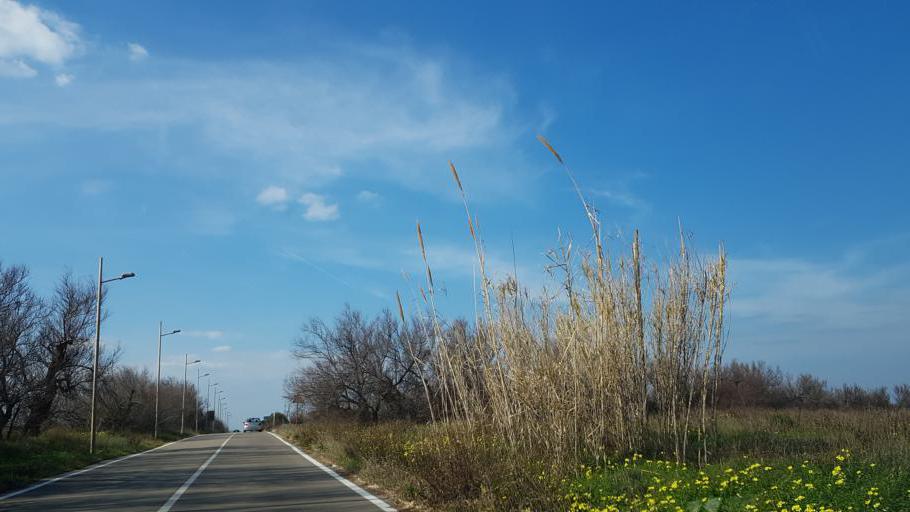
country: IT
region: Apulia
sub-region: Provincia di Brindisi
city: Brindisi
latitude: 40.6812
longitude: 17.8913
